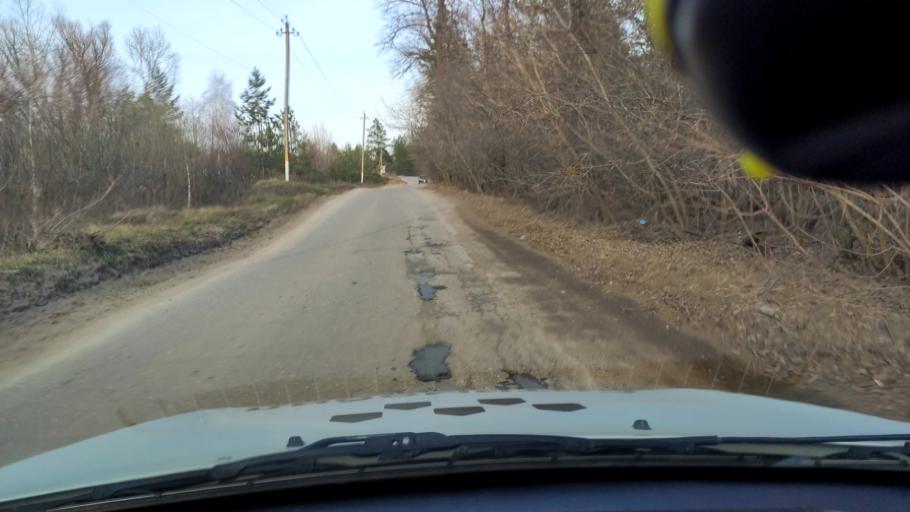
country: RU
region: Samara
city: Zhigulevsk
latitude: 53.4557
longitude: 49.5772
